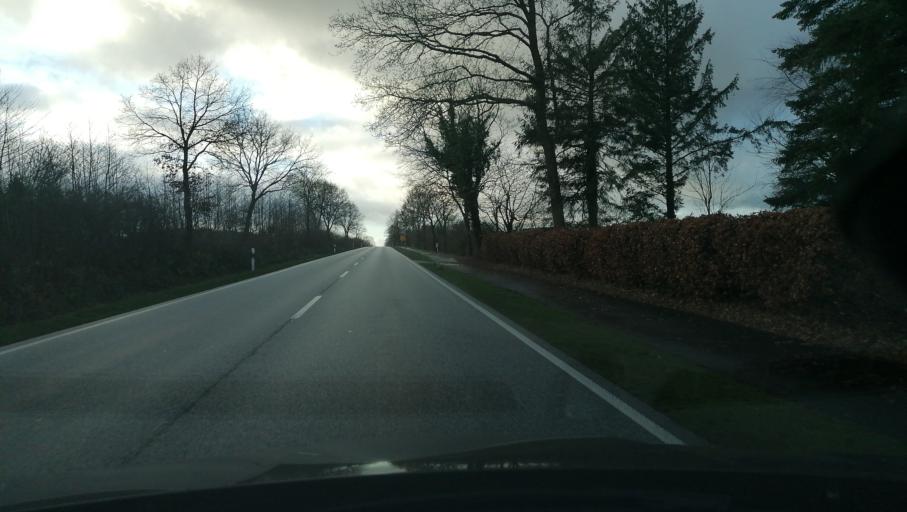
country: DE
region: Schleswig-Holstein
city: Tensbuttel-Rost
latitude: 54.1132
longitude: 9.2299
